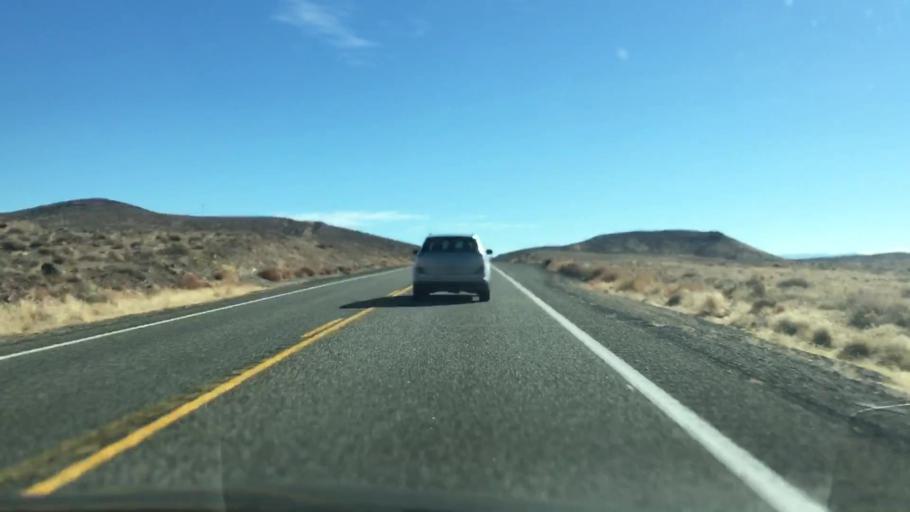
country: US
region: Nevada
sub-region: Lyon County
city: Silver Springs
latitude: 39.2311
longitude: -119.2303
